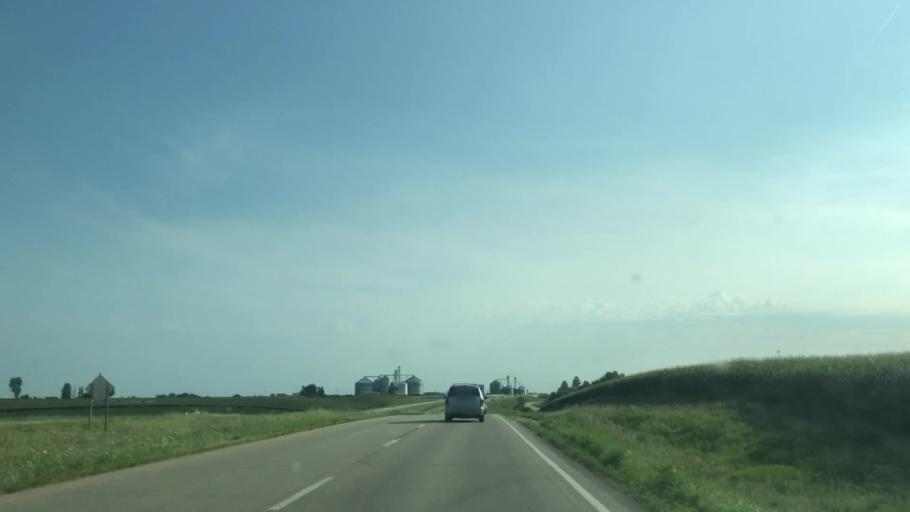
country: US
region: Iowa
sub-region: Marshall County
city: Marshalltown
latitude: 42.0155
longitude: -93.0145
